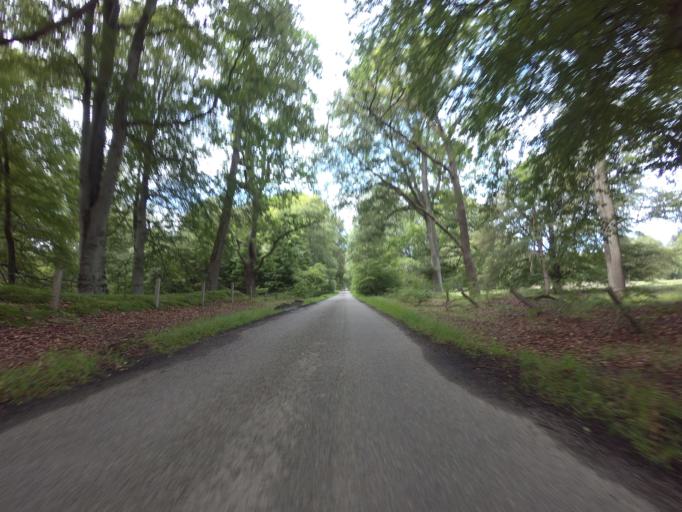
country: GB
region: Scotland
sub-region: Moray
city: Hopeman
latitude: 57.6708
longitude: -3.4139
